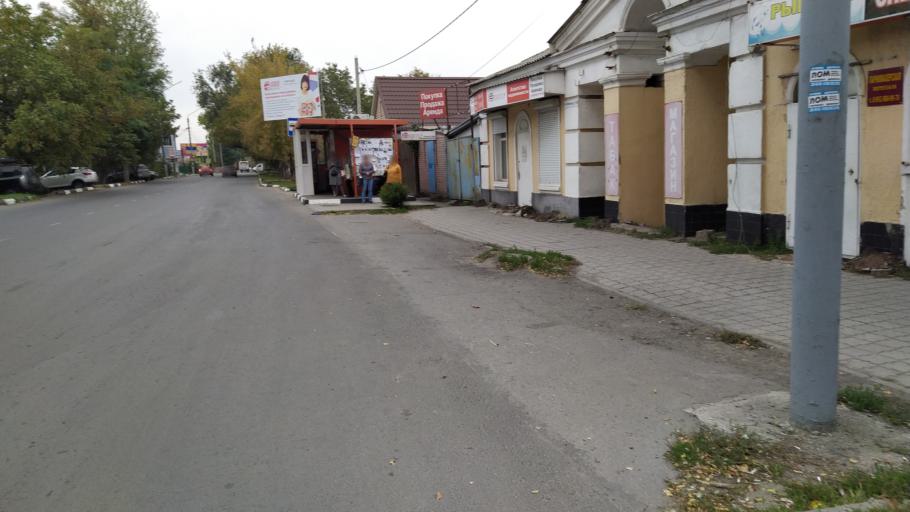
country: RU
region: Rostov
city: Bataysk
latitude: 47.1426
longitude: 39.7496
